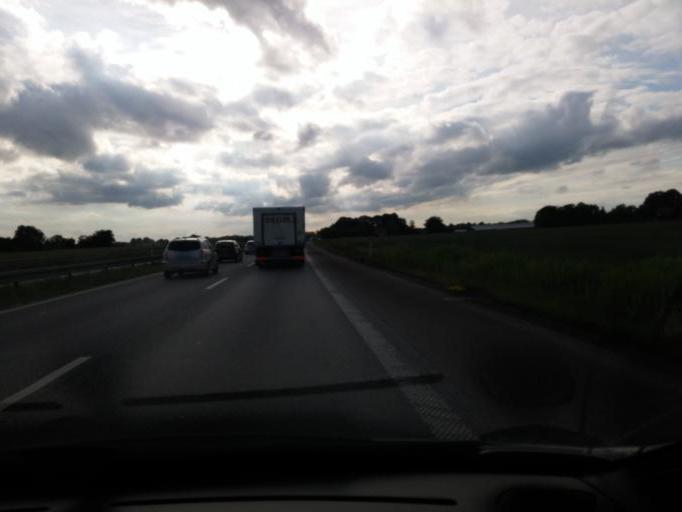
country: DK
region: Zealand
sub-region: Soro Kommune
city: Frederiksberg
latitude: 55.4488
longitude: 11.6351
